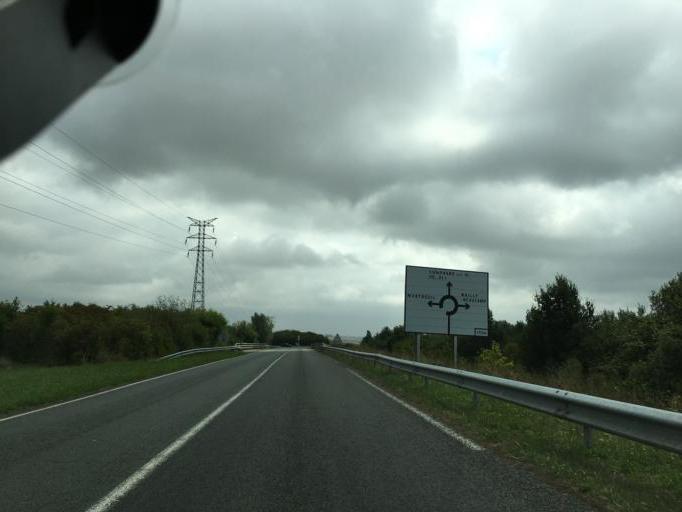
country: FR
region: Nord-Pas-de-Calais
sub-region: Departement du Pas-de-Calais
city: Montreuil
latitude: 50.4356
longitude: 1.7360
